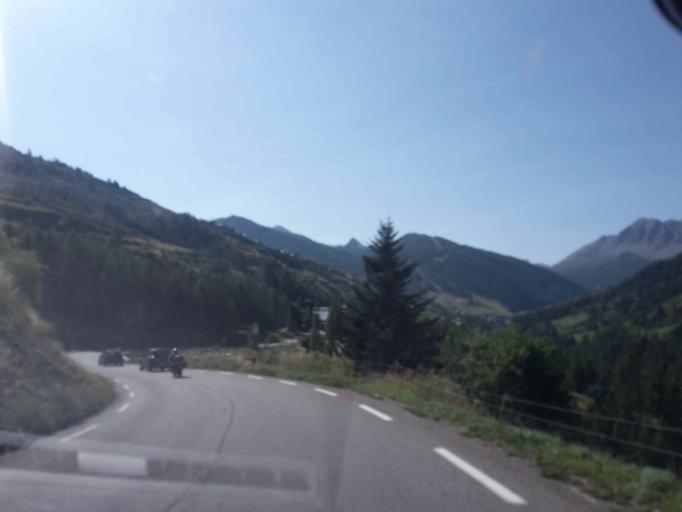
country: FR
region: Provence-Alpes-Cote d'Azur
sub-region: Departement des Hautes-Alpes
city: Guillestre
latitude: 44.6140
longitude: 6.6859
